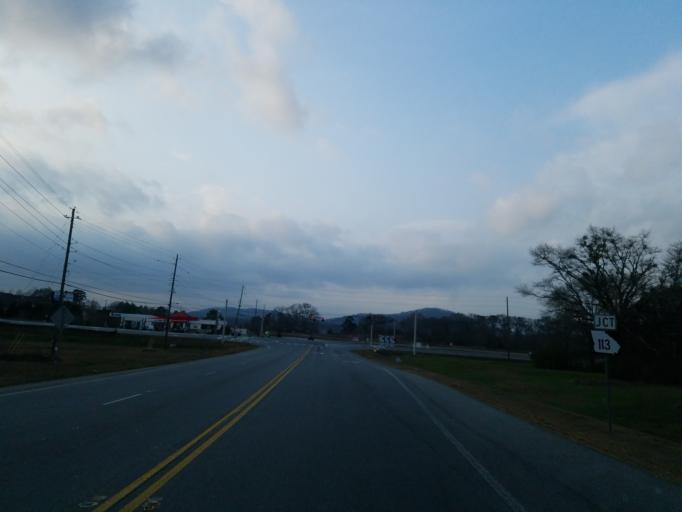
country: US
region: Georgia
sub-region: Bartow County
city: Cartersville
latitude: 34.1280
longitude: -84.8512
